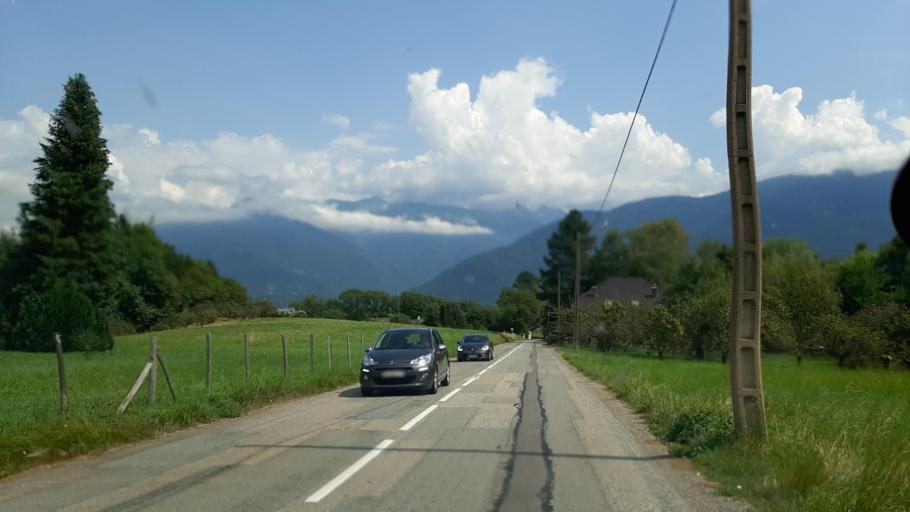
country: FR
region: Rhone-Alpes
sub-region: Departement de la Savoie
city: Frontenex
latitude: 45.6562
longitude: 6.3080
